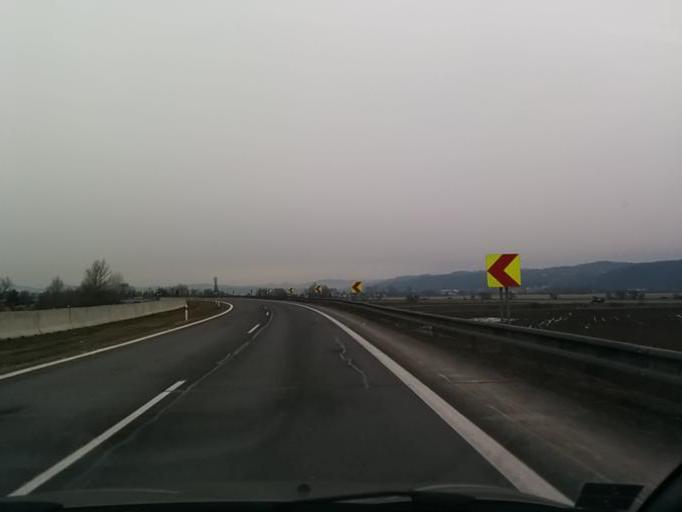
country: SK
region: Banskobystricky
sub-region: Okres Banska Bystrica
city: Zvolen
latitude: 48.6036
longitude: 19.1184
